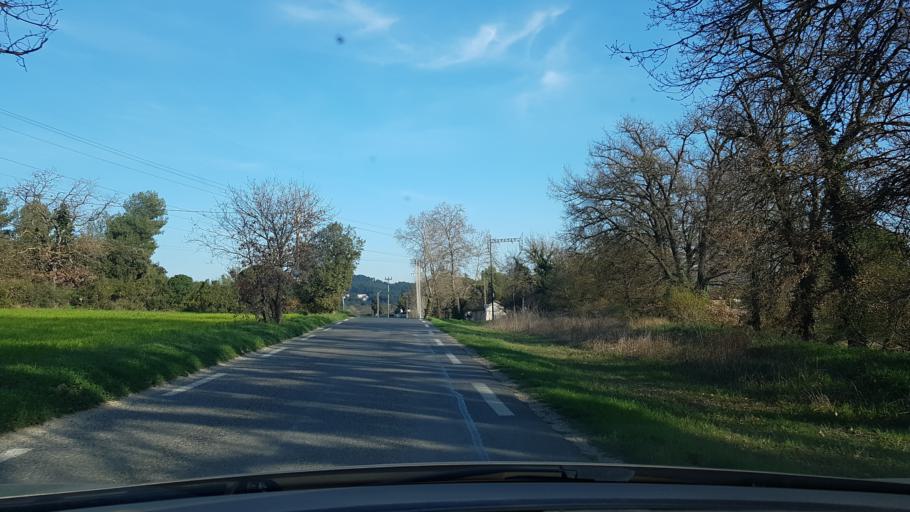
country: FR
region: Provence-Alpes-Cote d'Azur
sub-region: Departement des Bouches-du-Rhone
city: Cabries
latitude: 43.4563
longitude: 5.3836
